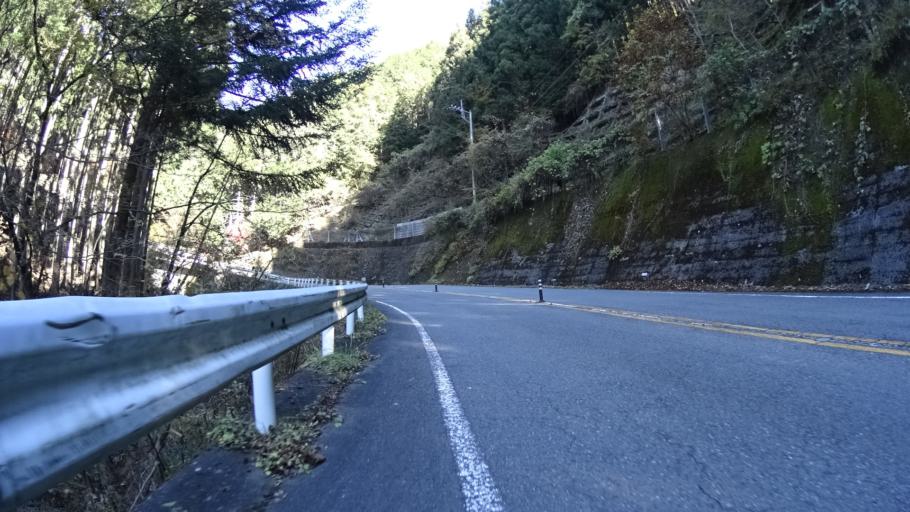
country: JP
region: Yamanashi
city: Otsuki
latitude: 35.7301
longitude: 138.9814
